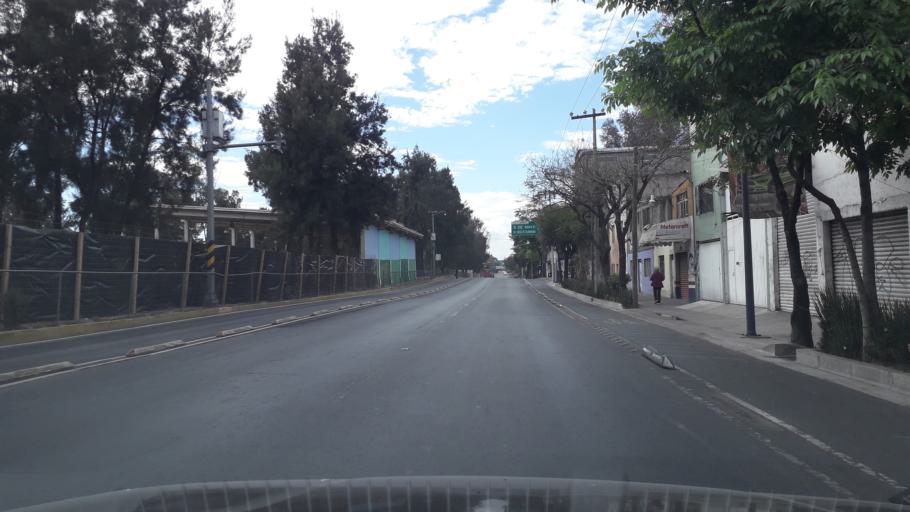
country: MX
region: Mexico City
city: Gustavo A. Madero
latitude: 19.4969
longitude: -99.0907
